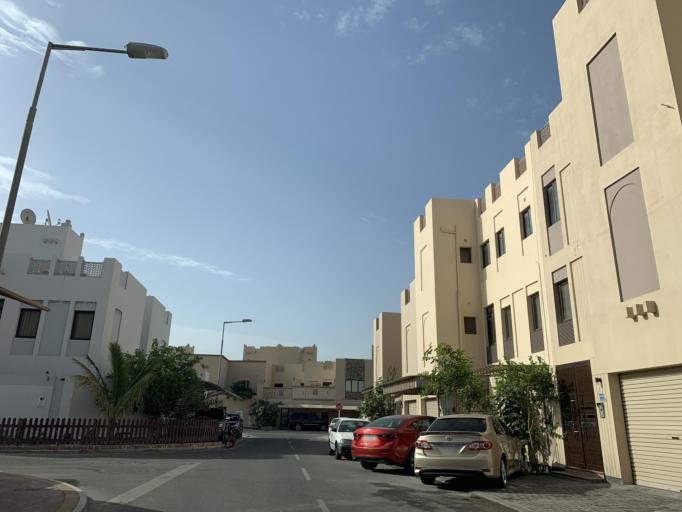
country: BH
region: Manama
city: Manama
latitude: 26.1808
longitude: 50.5893
